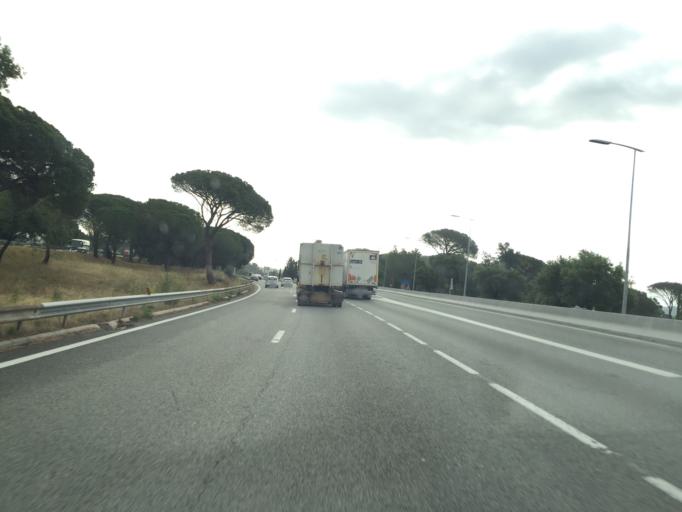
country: FR
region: Provence-Alpes-Cote d'Azur
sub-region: Departement du Var
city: Vidauban
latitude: 43.4135
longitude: 6.4486
